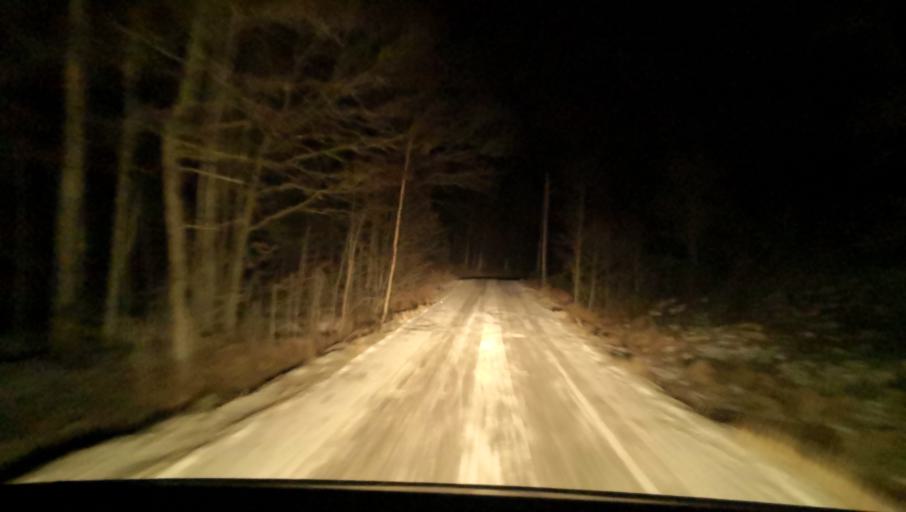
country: SE
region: Stockholm
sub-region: Tyreso Kommun
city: Bollmora
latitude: 59.2778
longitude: 18.2294
